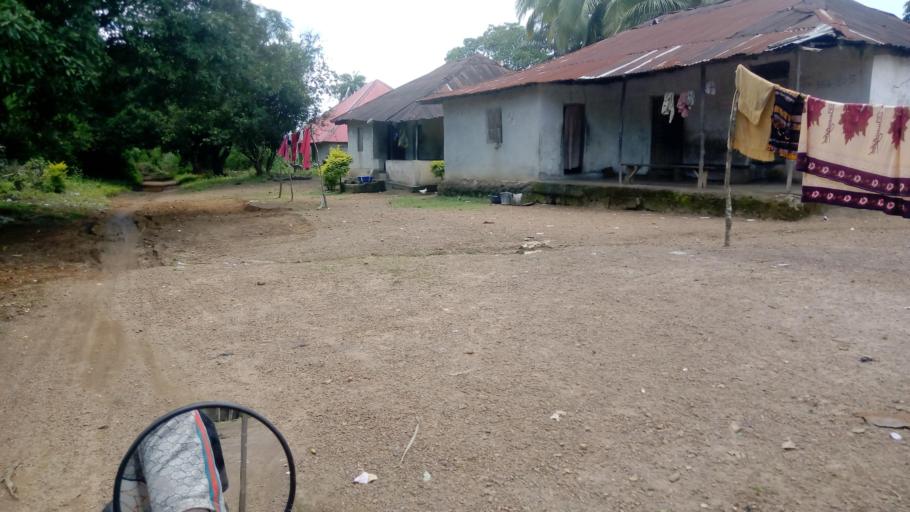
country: SL
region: Northern Province
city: Binkolo
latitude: 8.9280
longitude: -12.0081
